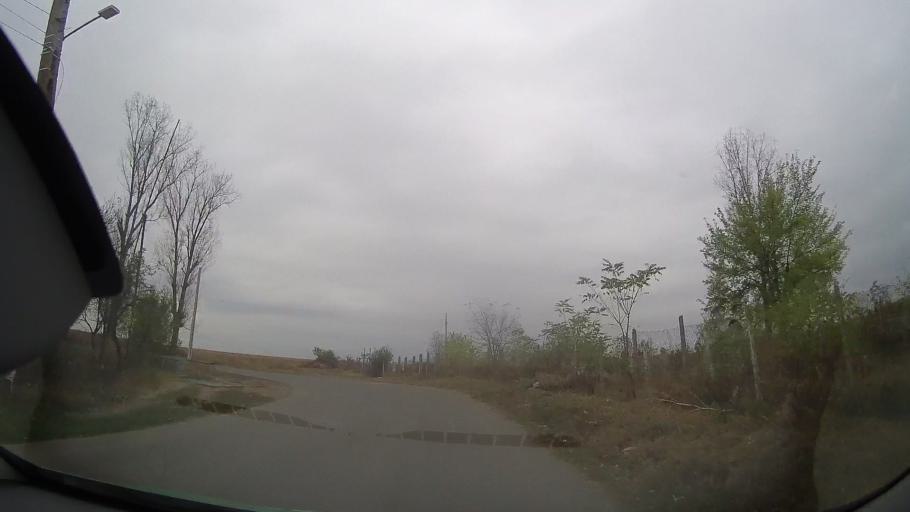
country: RO
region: Braila
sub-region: Comuna Ciocile
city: Ciocile
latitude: 44.8076
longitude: 27.2783
